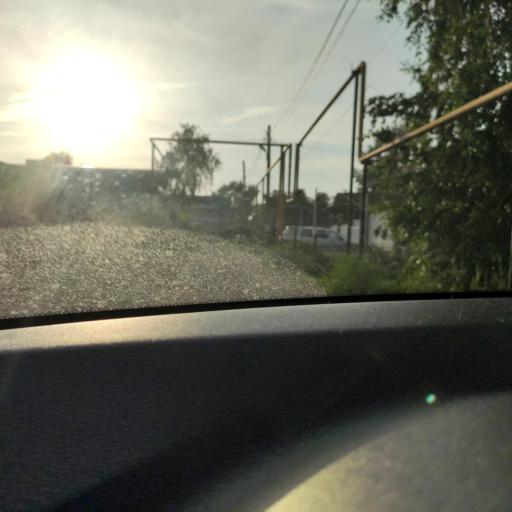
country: RU
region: Samara
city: Rozhdestveno
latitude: 53.1514
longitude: 50.0232
